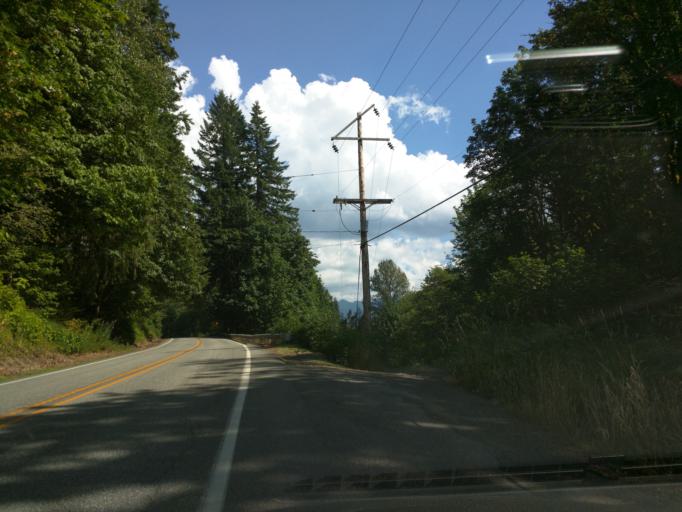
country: US
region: Washington
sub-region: Whatcom County
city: Peaceful Valley
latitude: 48.9262
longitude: -122.0210
